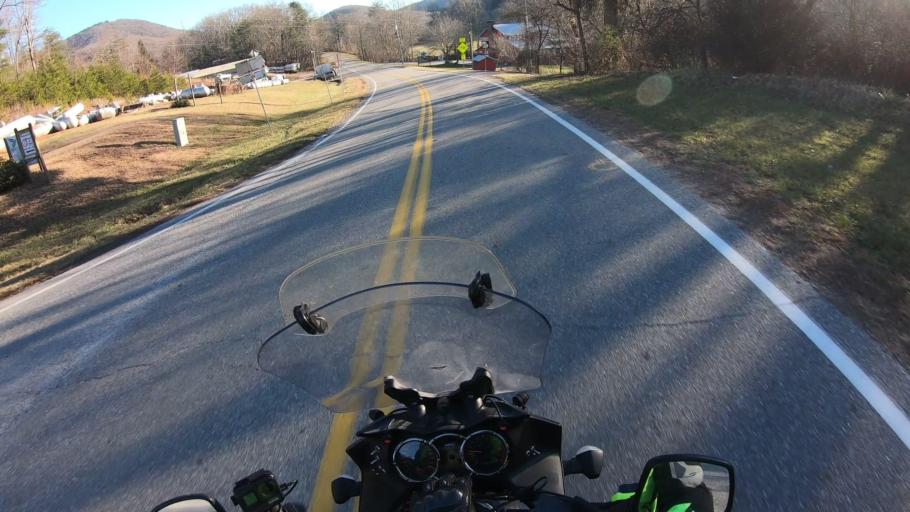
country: US
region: Georgia
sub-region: Lumpkin County
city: Dahlonega
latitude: 34.6986
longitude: -84.0284
